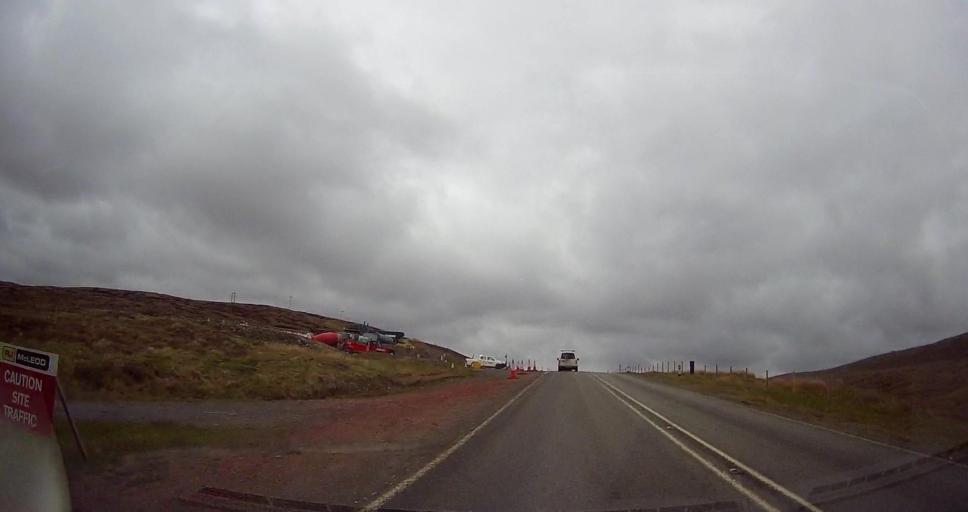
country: GB
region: Scotland
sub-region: Shetland Islands
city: Lerwick
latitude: 60.3269
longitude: -1.2531
